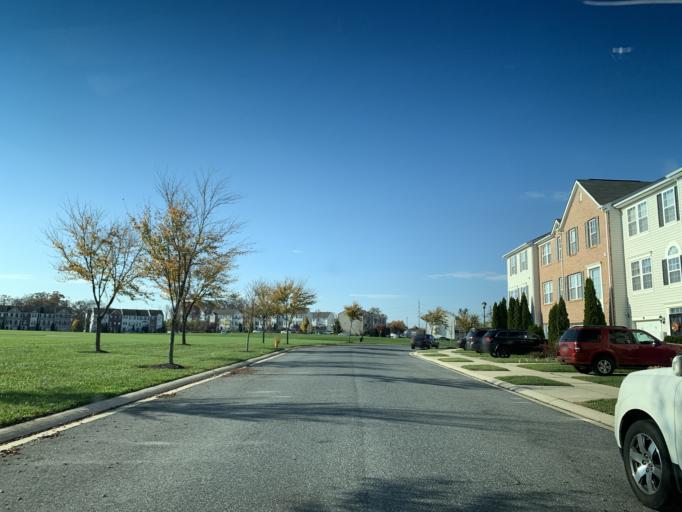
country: US
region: Maryland
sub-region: Baltimore County
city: Middle River
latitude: 39.3474
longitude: -76.4464
